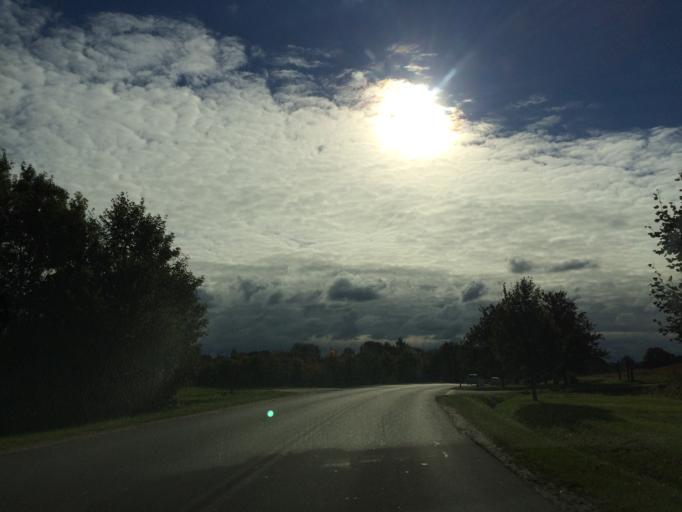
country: DK
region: Central Jutland
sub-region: Skanderborg Kommune
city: Ry
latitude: 56.0797
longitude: 9.7061
